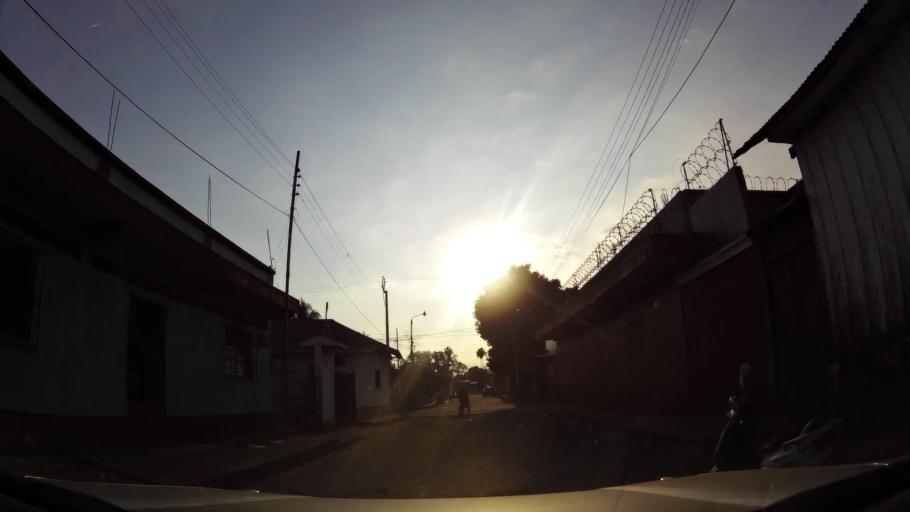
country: GT
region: Retalhuleu
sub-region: Municipio de Retalhuleu
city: Retalhuleu
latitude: 14.5412
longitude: -91.6782
